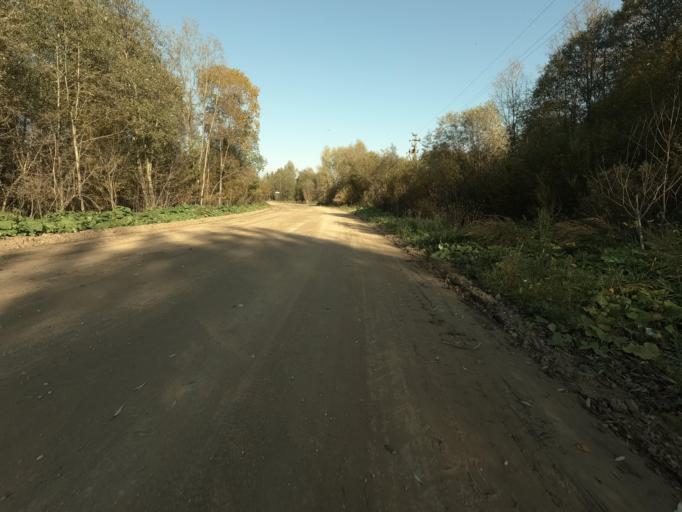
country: RU
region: Novgorod
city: Batetskiy
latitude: 58.8794
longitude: 30.7273
